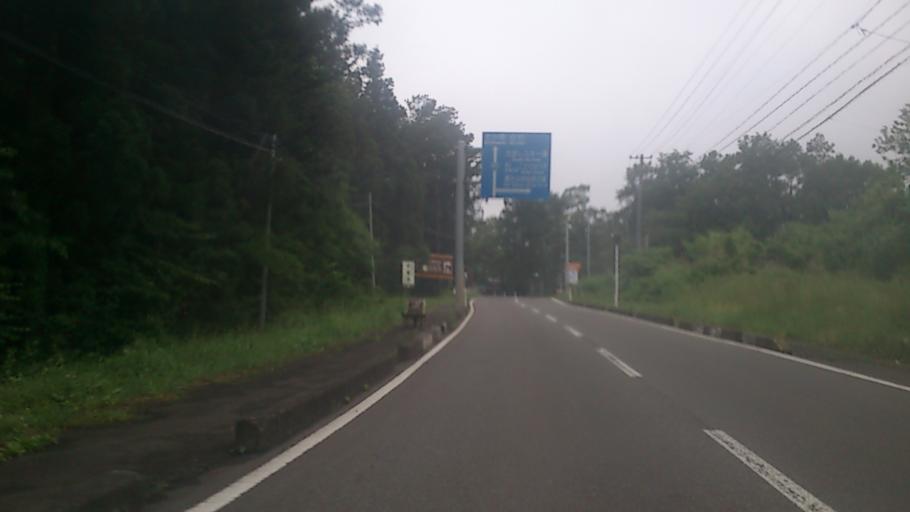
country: JP
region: Miyagi
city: Shiroishi
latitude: 38.1133
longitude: 140.5663
